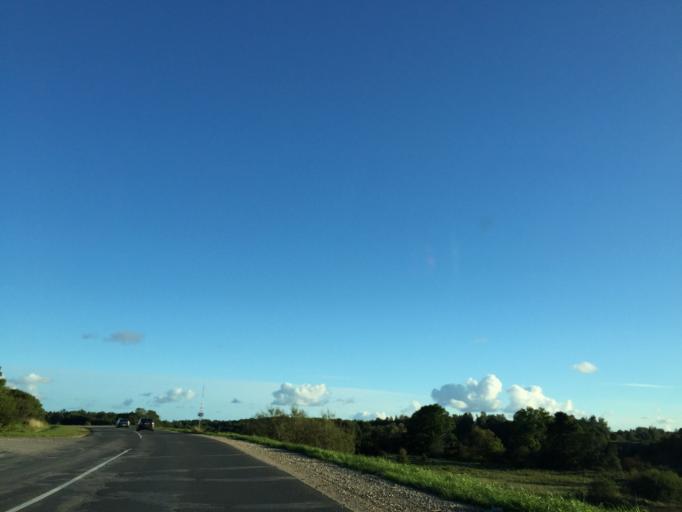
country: LV
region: Kuldigas Rajons
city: Kuldiga
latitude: 56.9595
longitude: 22.0037
